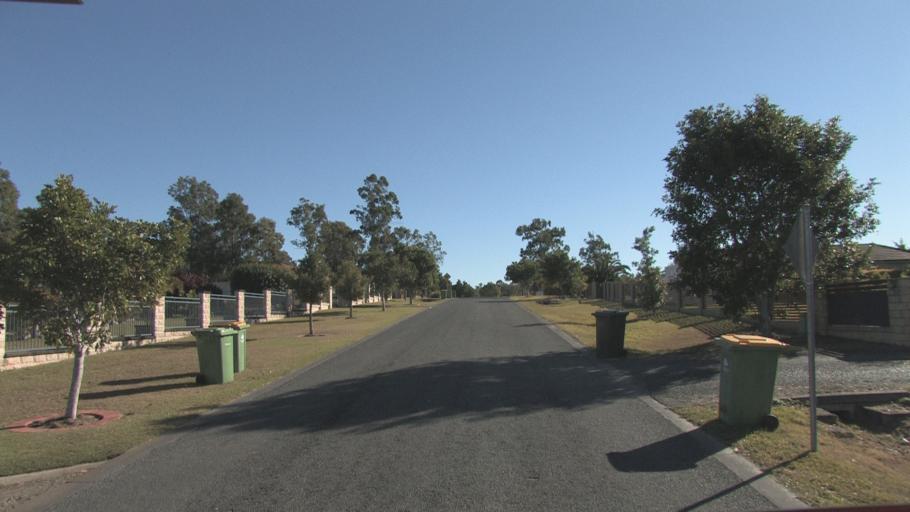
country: AU
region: Queensland
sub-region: Logan
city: North Maclean
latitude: -27.7483
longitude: 152.9585
